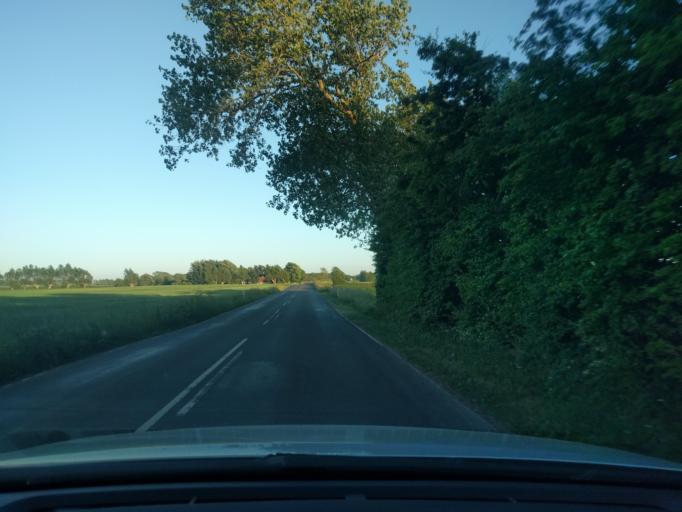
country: DK
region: South Denmark
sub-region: Kerteminde Kommune
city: Kerteminde
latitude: 55.5612
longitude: 10.6497
